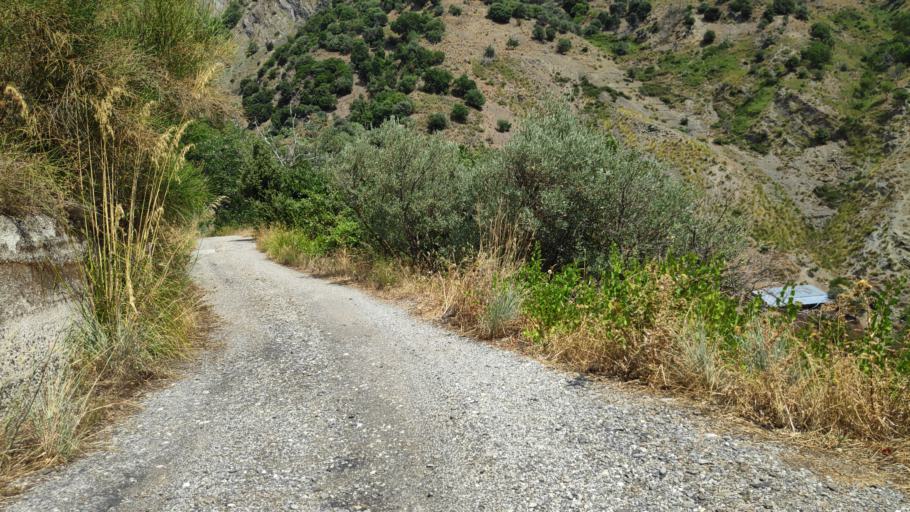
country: IT
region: Calabria
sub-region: Provincia di Reggio Calabria
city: Bivongi
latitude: 38.4920
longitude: 16.4532
